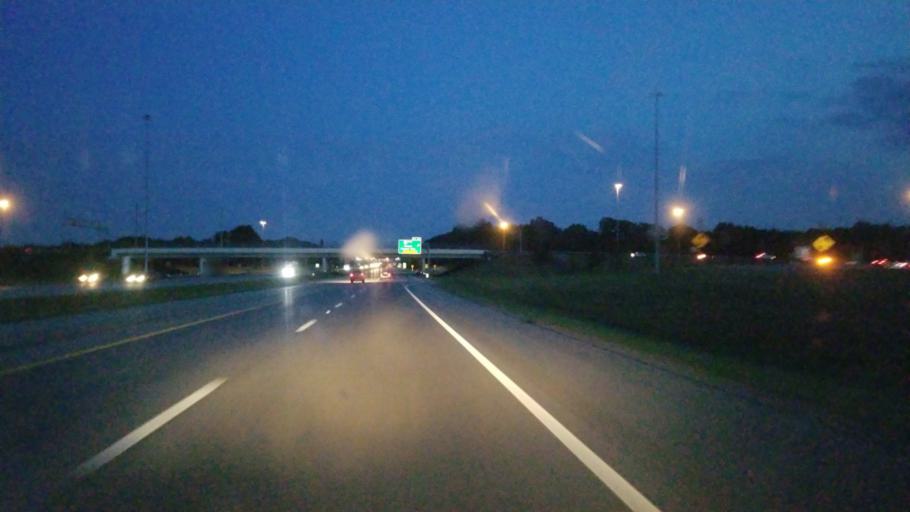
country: US
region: Ohio
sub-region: Lucas County
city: Holland
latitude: 41.6149
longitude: -83.6916
